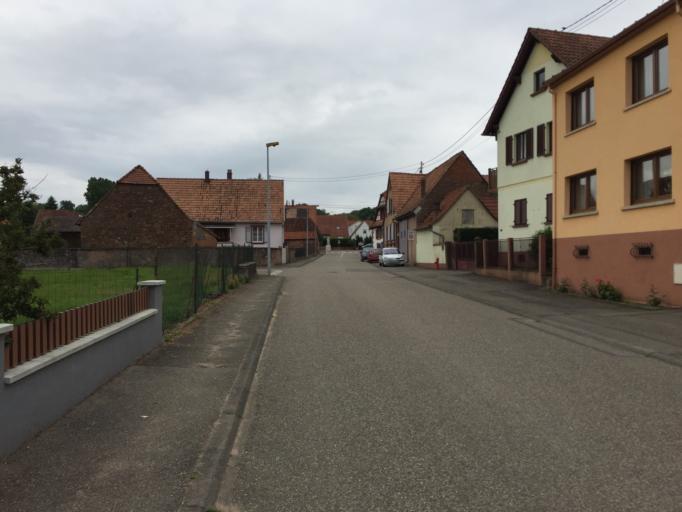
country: FR
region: Alsace
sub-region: Departement du Bas-Rhin
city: Gundershoffen
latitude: 48.9052
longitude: 7.6630
